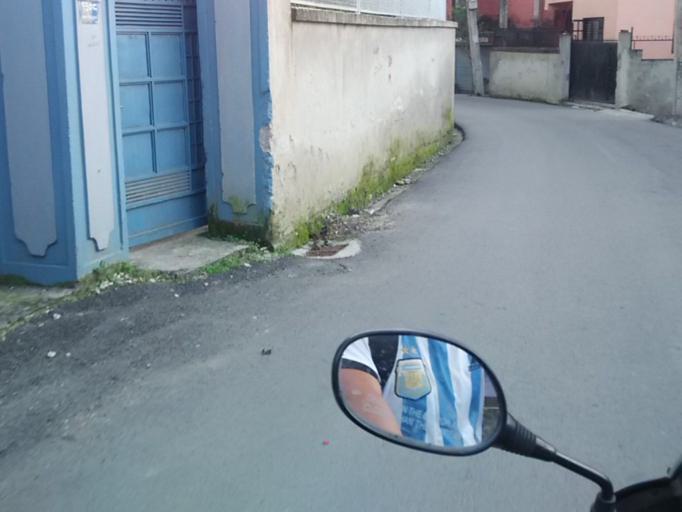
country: NP
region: Central Region
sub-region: Bagmati Zone
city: Kathmandu
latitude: 27.7328
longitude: 85.3361
